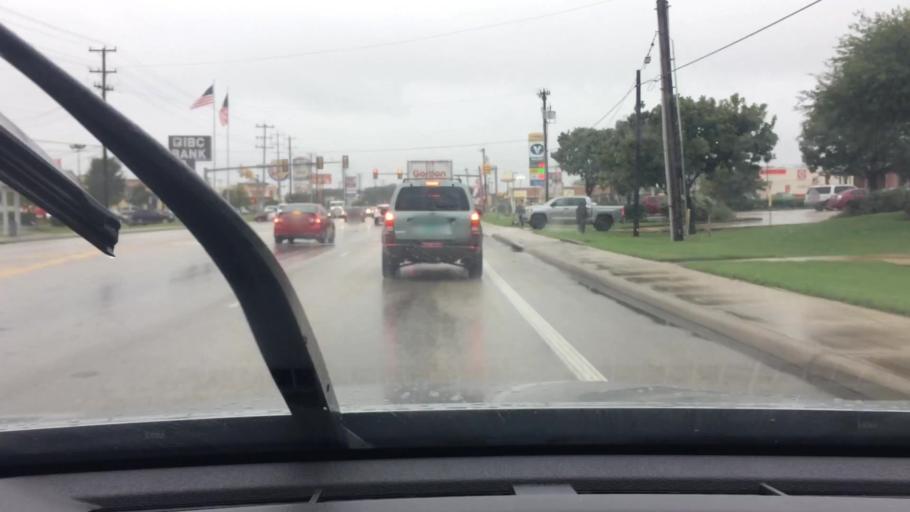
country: US
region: Texas
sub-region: Bexar County
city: Helotes
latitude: 29.4957
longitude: -98.7086
